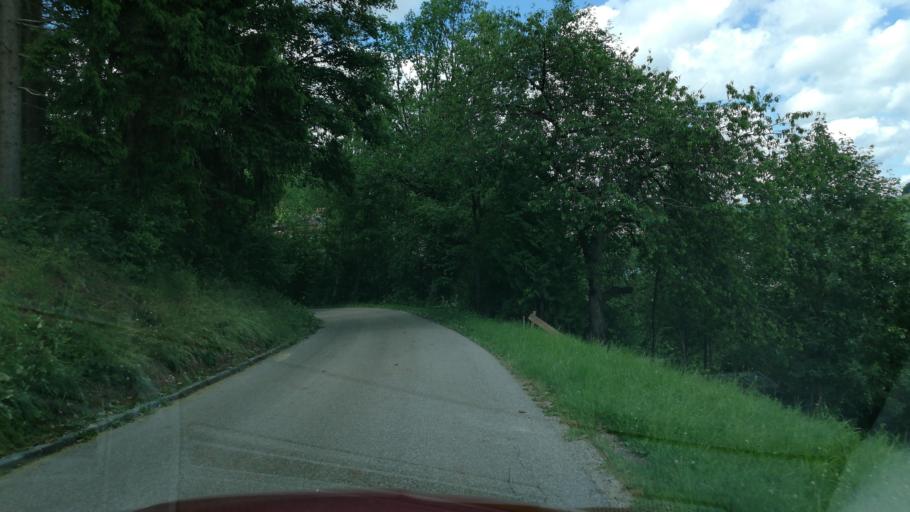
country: AT
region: Upper Austria
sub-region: Politischer Bezirk Urfahr-Umgebung
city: Reichenau im Muhlkreis
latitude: 48.4541
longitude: 14.3491
